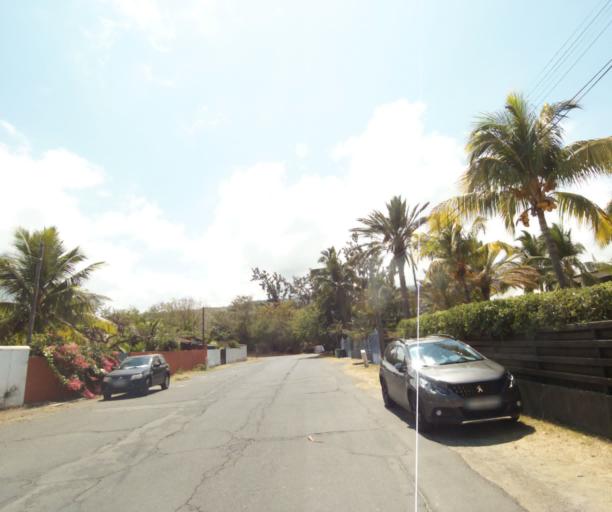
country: RE
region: Reunion
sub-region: Reunion
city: Trois-Bassins
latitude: -21.0910
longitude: 55.2341
